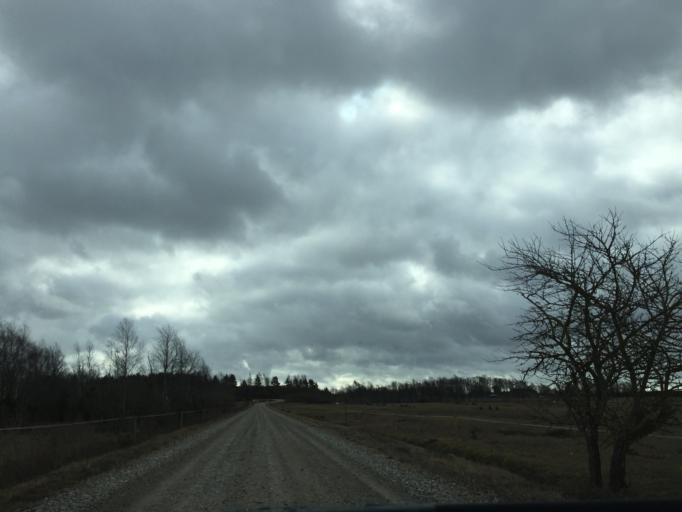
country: EE
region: Laeaene
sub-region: Haapsalu linn
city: Haapsalu
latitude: 58.6803
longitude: 23.5354
